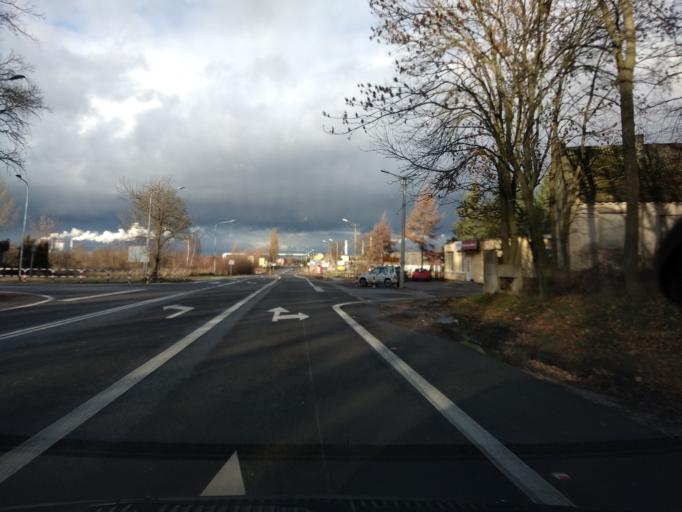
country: PL
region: Greater Poland Voivodeship
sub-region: Konin
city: Konin
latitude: 52.2645
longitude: 18.2676
